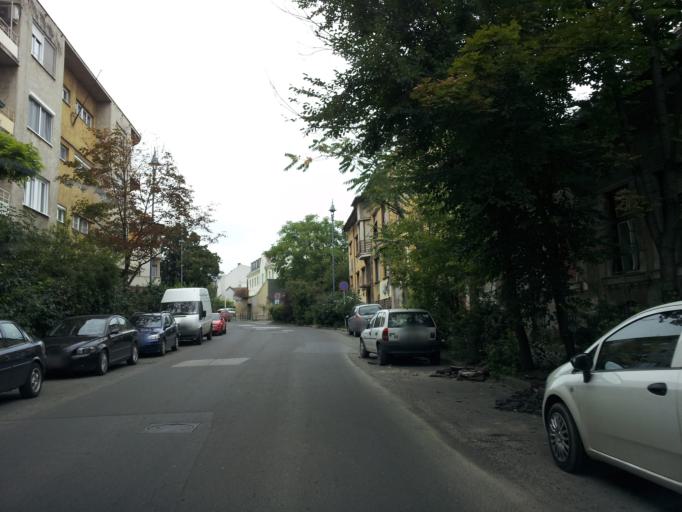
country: HU
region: Budapest
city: Budapest II. keruelet
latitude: 47.5258
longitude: 19.0359
